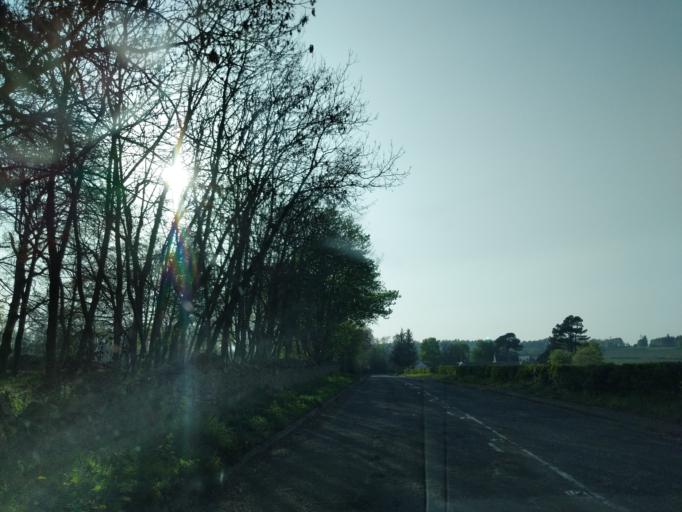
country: GB
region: Scotland
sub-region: Fife
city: Pathhead
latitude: 55.8700
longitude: -2.9858
